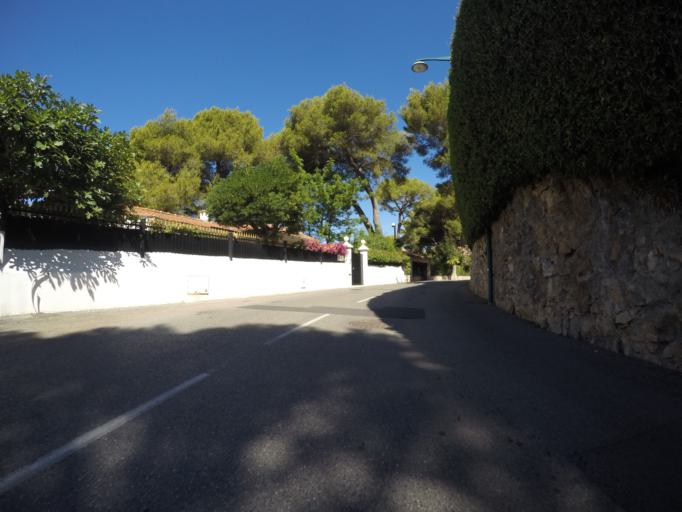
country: FR
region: Provence-Alpes-Cote d'Azur
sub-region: Departement des Alpes-Maritimes
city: Saint-Jean-Cap-Ferrat
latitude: 43.6859
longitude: 7.3247
